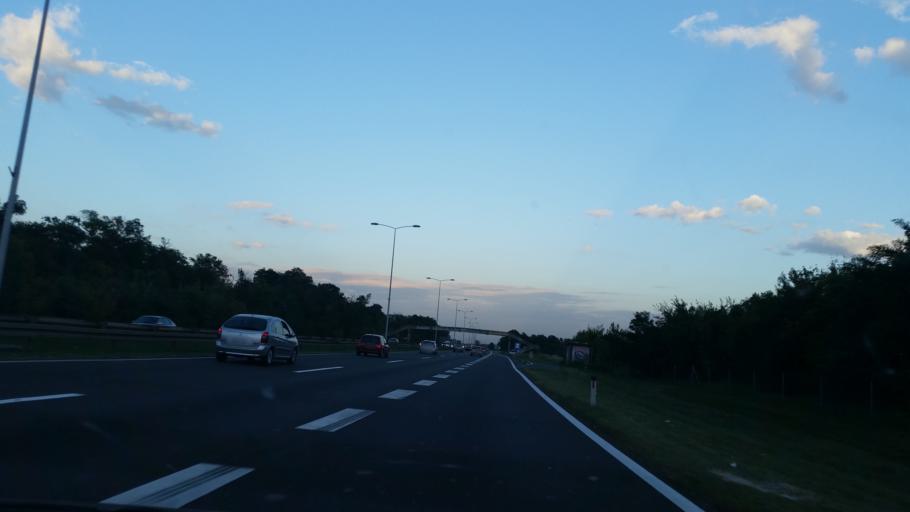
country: RS
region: Central Serbia
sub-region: Belgrade
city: Surcin
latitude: 44.8334
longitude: 20.2832
